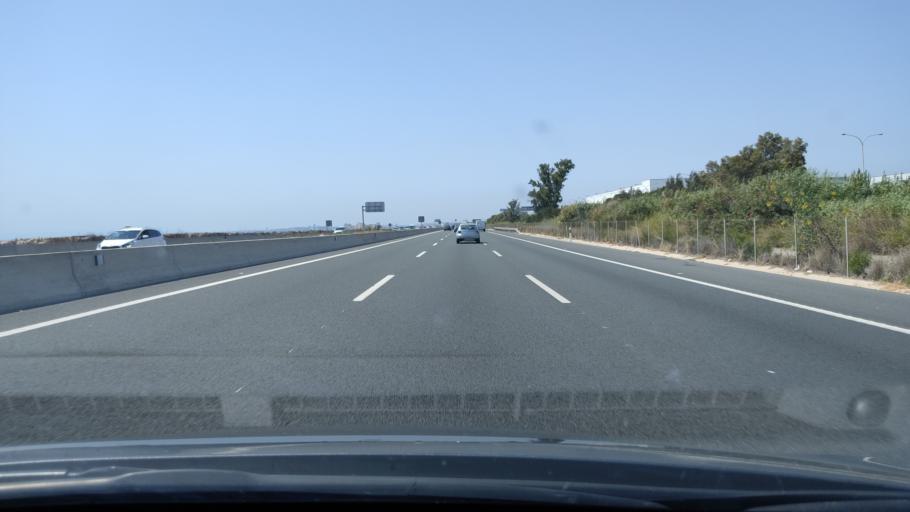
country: ES
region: Valencia
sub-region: Provincia de Valencia
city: Albuixech
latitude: 39.5453
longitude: -0.3004
